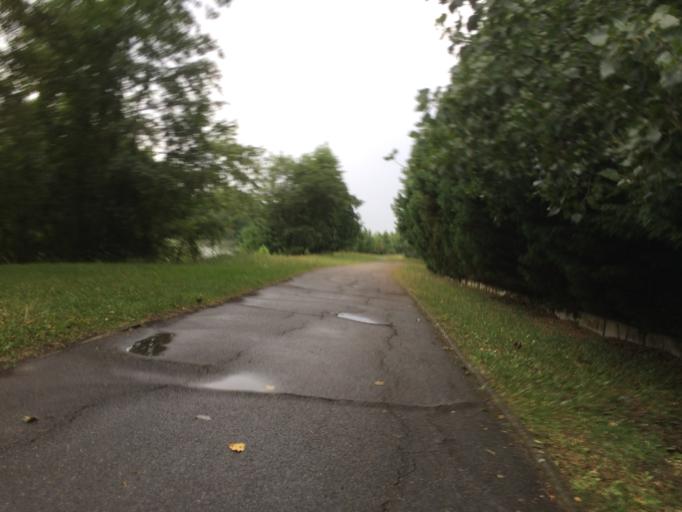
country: FR
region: Picardie
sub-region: Departement de l'Oise
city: Jaux
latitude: 49.3866
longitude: 2.7802
